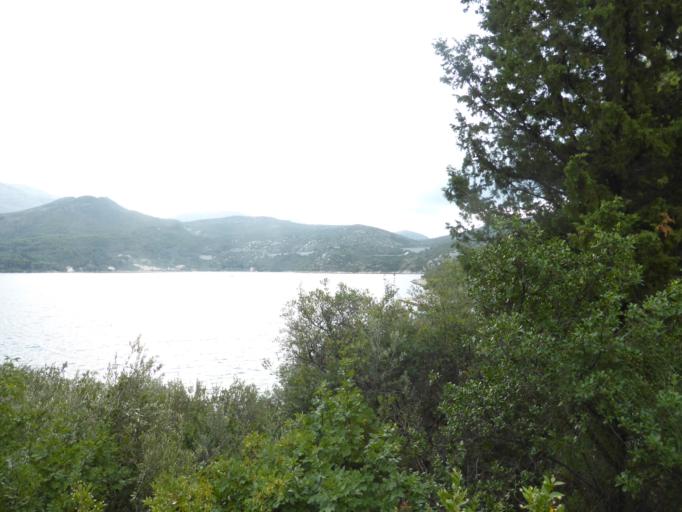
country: HR
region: Dubrovacko-Neretvanska
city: Podgora
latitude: 42.7790
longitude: 17.8692
